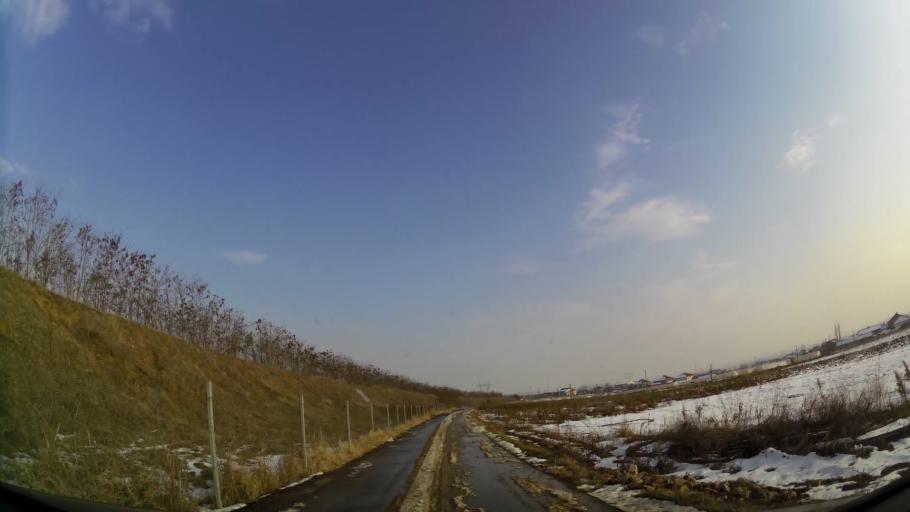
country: MK
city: Creshevo
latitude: 42.0333
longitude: 21.5227
